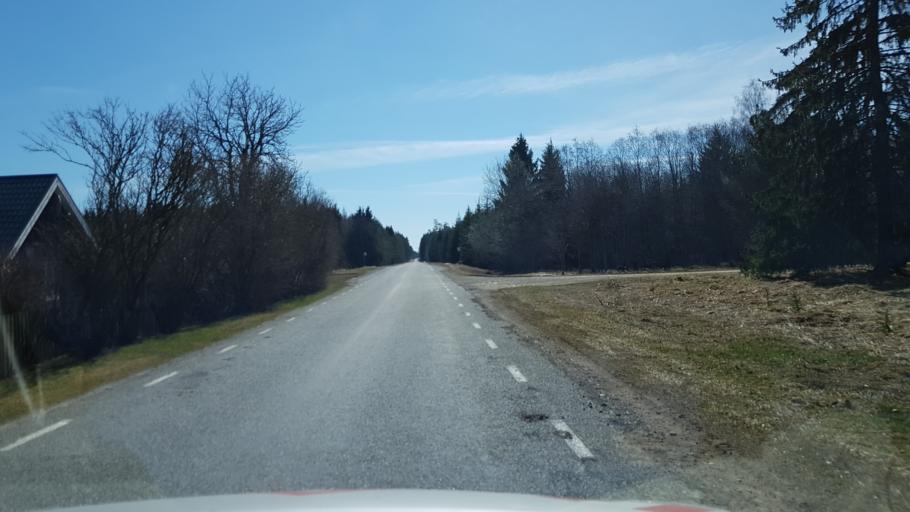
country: EE
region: Laeaene-Virumaa
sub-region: Vinni vald
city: Vinni
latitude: 59.1620
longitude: 26.5121
